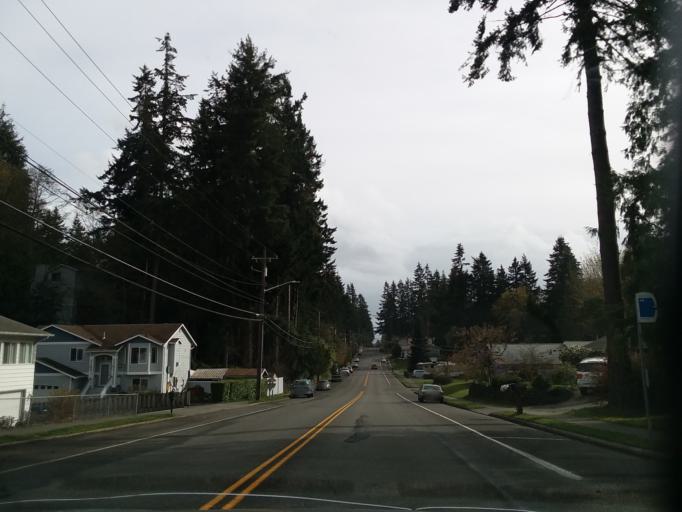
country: US
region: Washington
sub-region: Snohomish County
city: Mountlake Terrace
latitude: 47.7957
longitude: -122.3220
